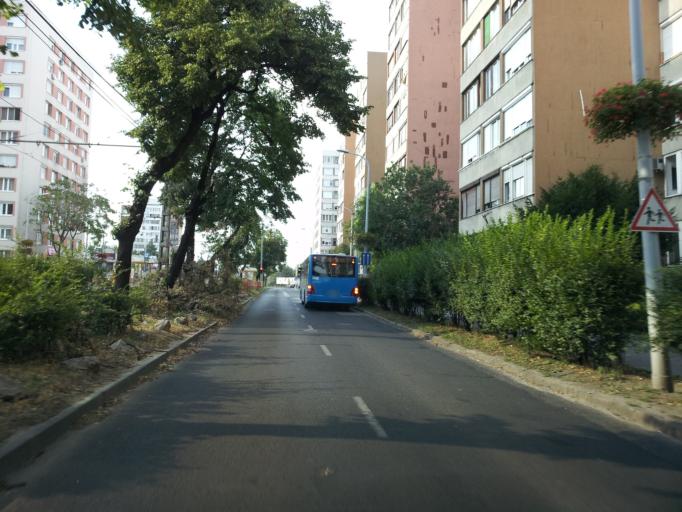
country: HU
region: Budapest
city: Budapest XXII. keruelet
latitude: 47.4316
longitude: 19.0374
